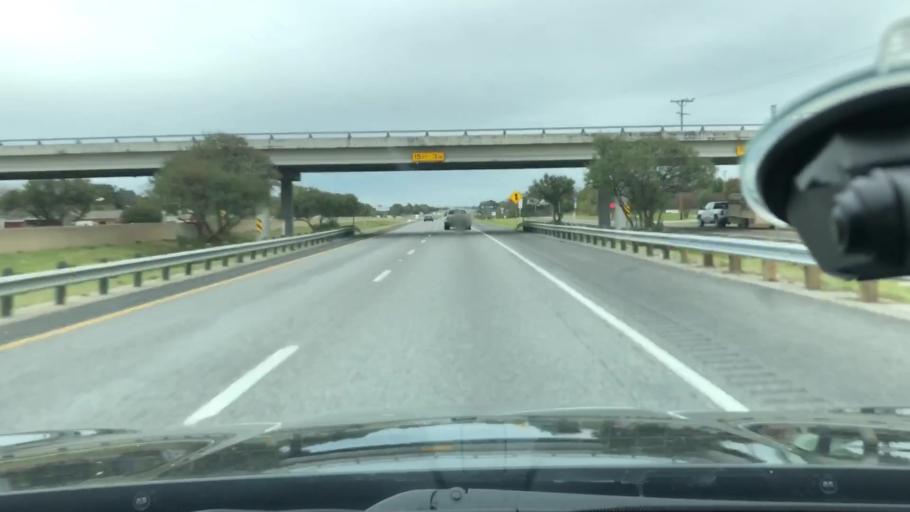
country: US
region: Texas
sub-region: Hunt County
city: Greenville
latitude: 33.1332
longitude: -96.0568
